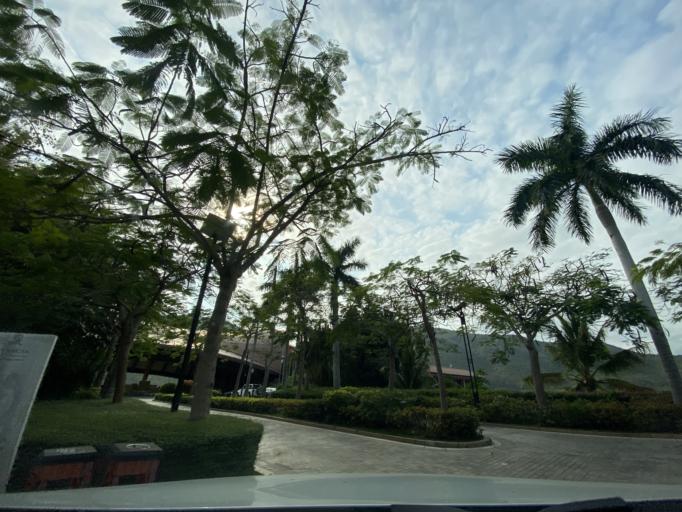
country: CN
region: Hainan
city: Tiandu
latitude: 18.2192
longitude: 109.6124
